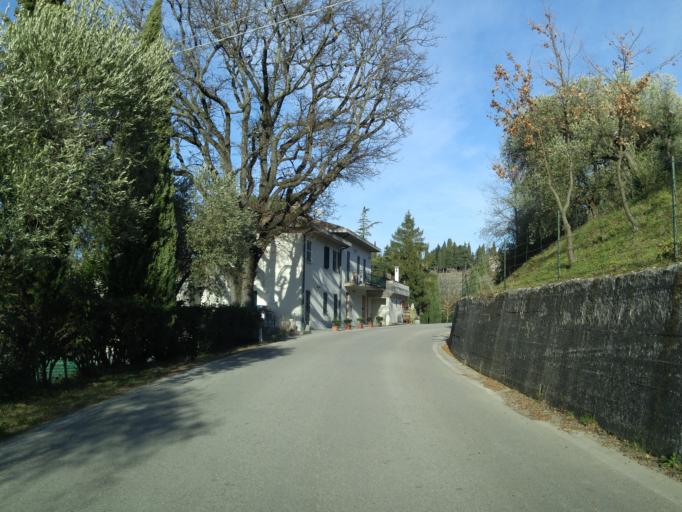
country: IT
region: The Marches
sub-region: Provincia di Pesaro e Urbino
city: Cartoceto
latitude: 43.7676
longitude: 12.8909
